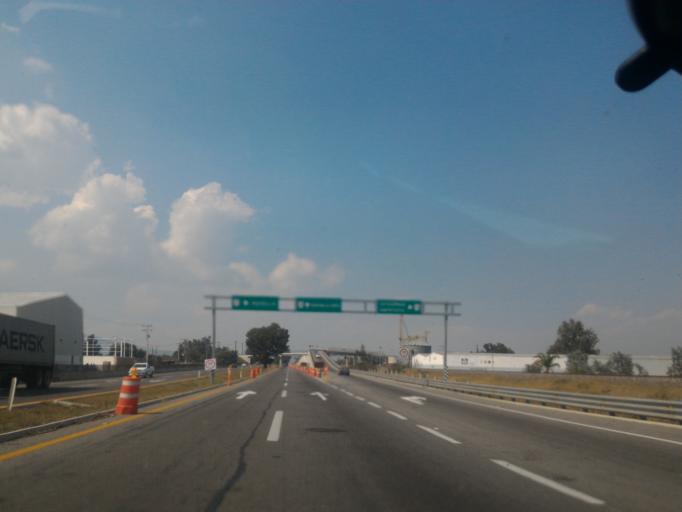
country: MX
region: Jalisco
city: Ciudad Guzman
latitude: 19.6972
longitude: -103.4963
